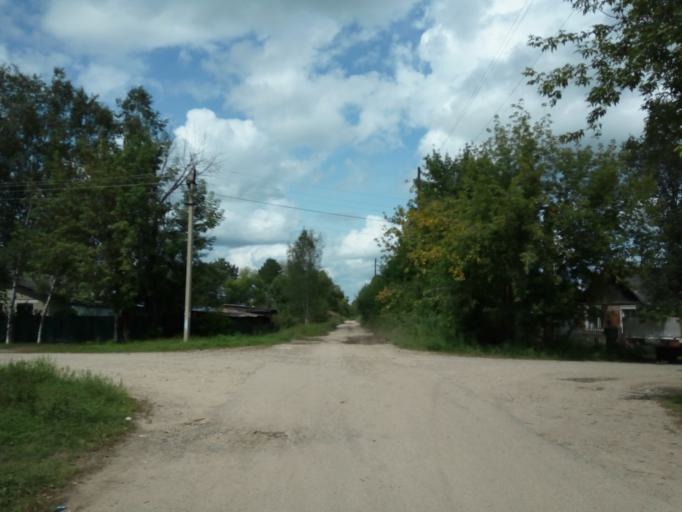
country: RU
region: Primorskiy
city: Dal'nerechensk
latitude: 45.9517
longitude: 133.8082
